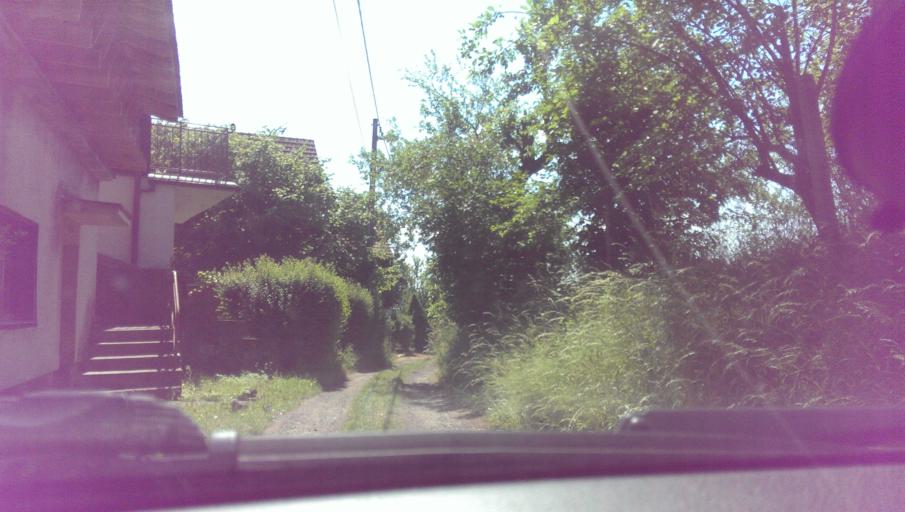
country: CZ
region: Zlin
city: Kunovice
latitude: 49.0682
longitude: 17.4907
